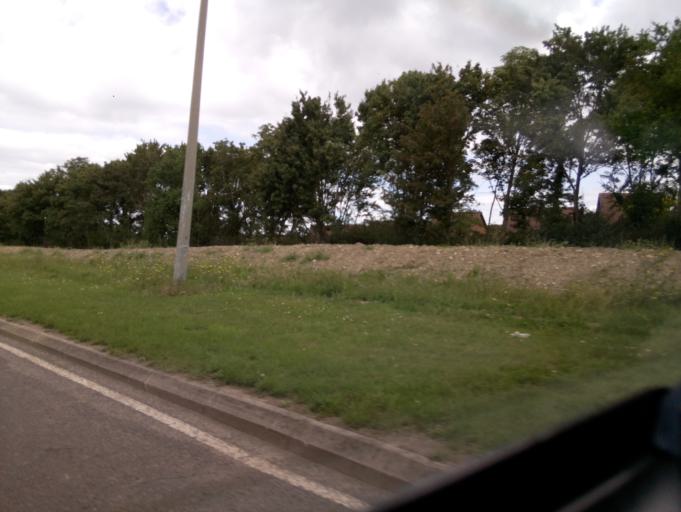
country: GB
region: England
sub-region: Milton Keynes
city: Shenley Church End
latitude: 52.0200
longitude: -0.7968
